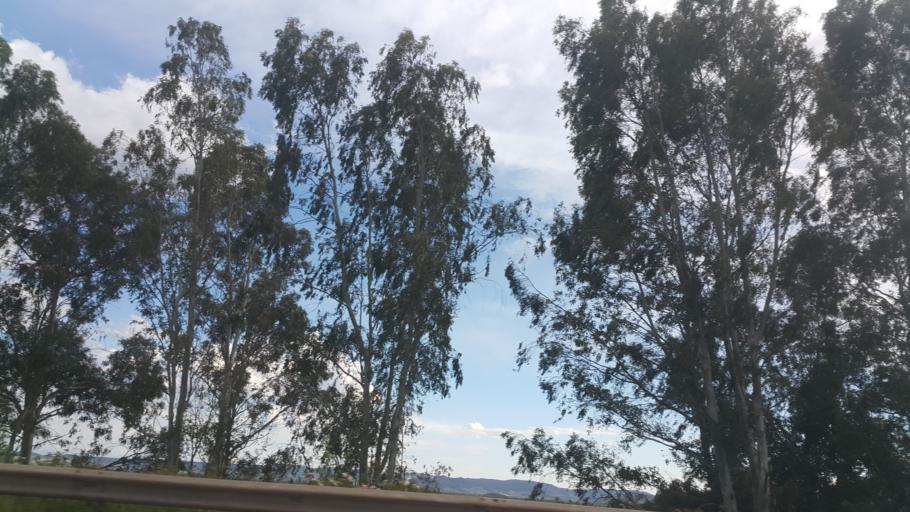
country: TR
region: Adana
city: Ceyhan
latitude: 36.9873
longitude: 35.7566
